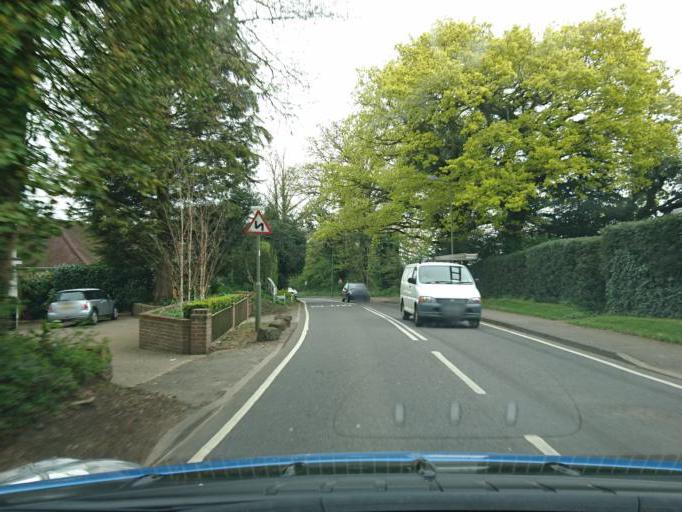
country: GB
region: England
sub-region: Greater London
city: Barnet
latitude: 51.6360
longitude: -0.1984
